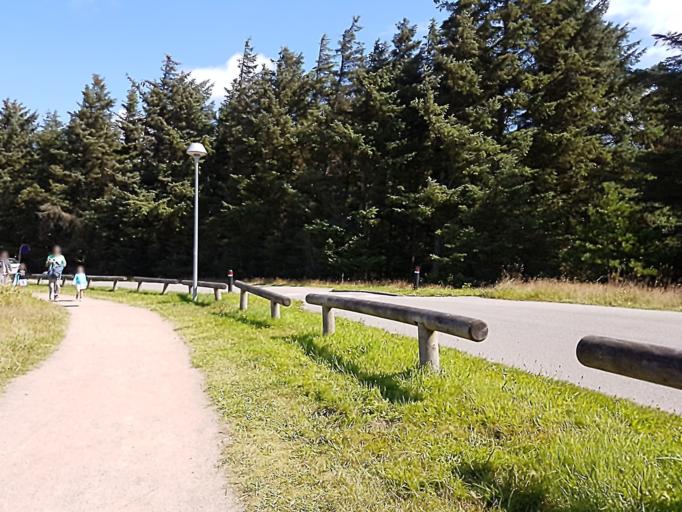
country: DK
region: South Denmark
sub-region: Varde Kommune
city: Oksbol
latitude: 55.8434
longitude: 8.2758
